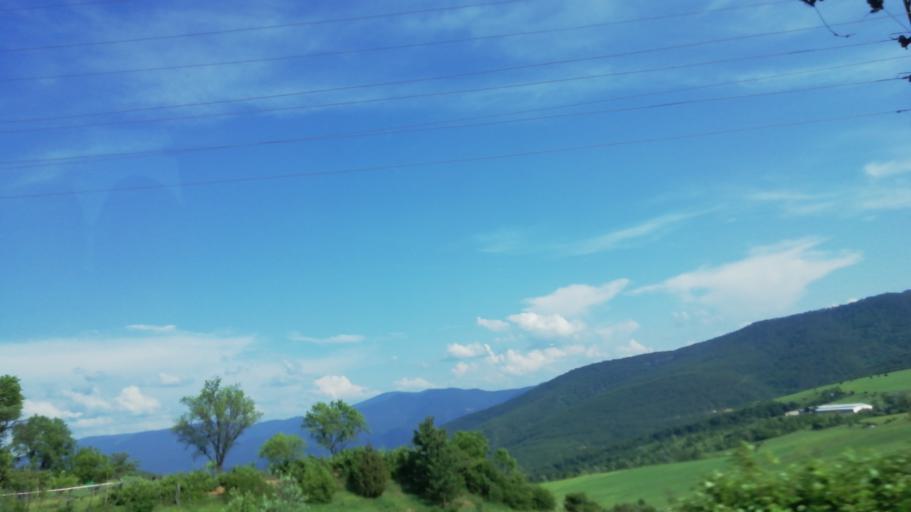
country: TR
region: Karabuk
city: Karabuk
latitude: 41.1042
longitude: 32.5954
